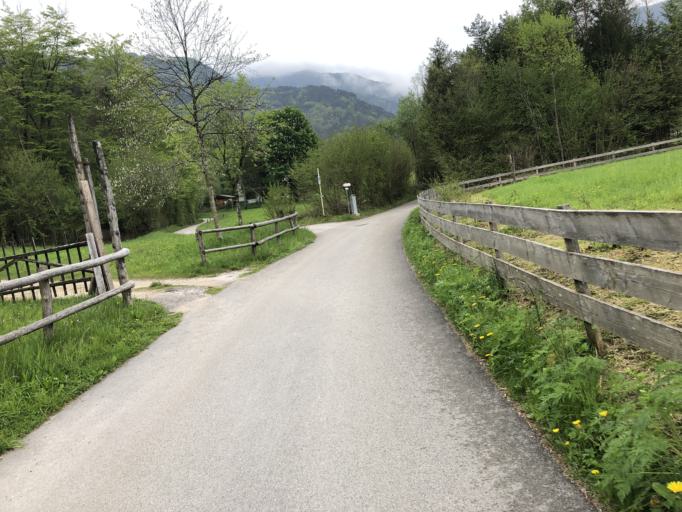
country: IT
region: Trentino-Alto Adige
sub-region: Provincia di Trento
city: Molina di Ledro
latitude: 45.8641
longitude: 10.7470
